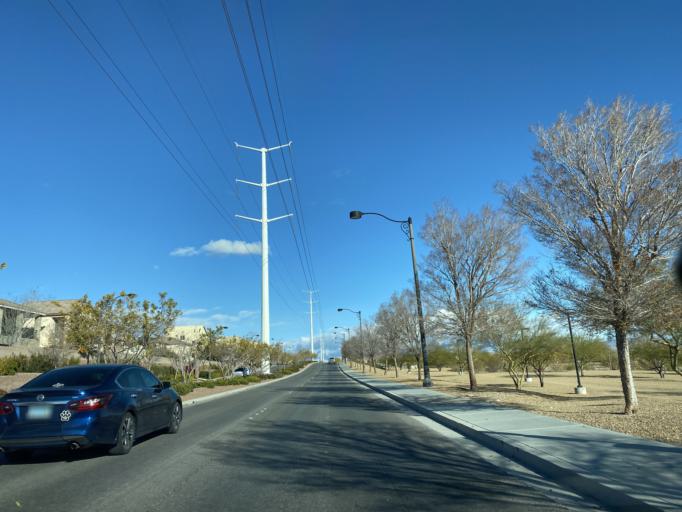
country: US
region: Nevada
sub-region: Clark County
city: Summerlin South
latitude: 36.2853
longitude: -115.3288
